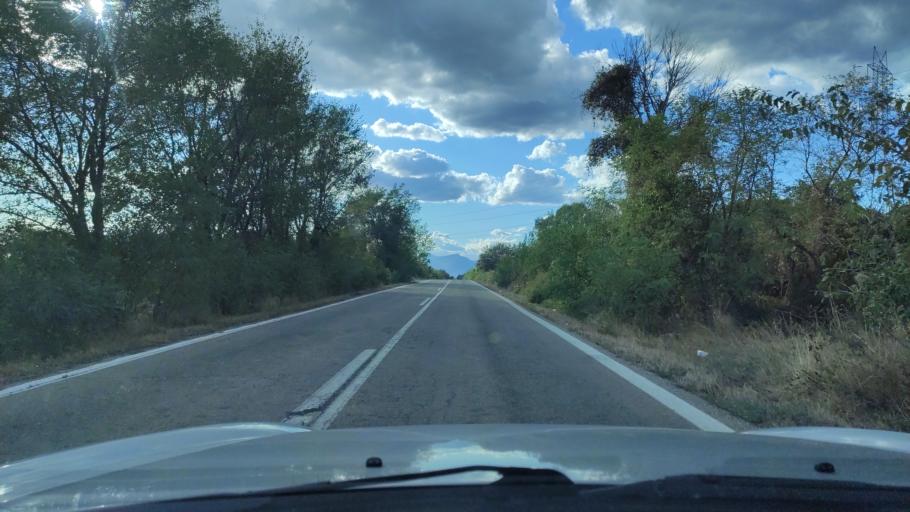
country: GR
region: East Macedonia and Thrace
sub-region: Nomos Rodopis
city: Iasmos
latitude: 41.1190
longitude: 25.1031
